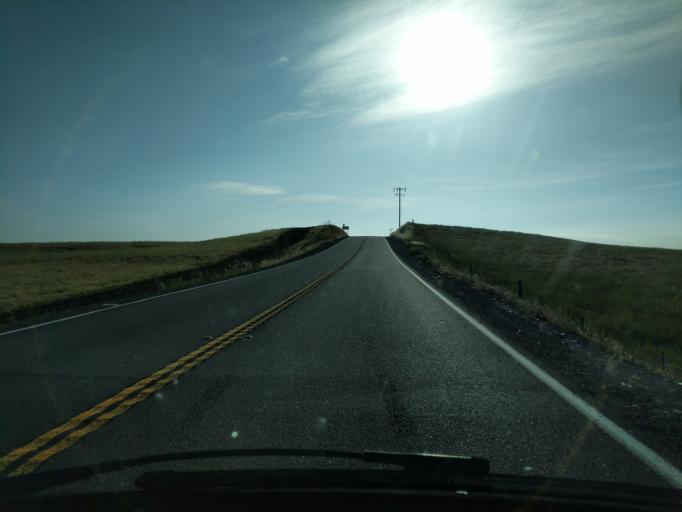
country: US
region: California
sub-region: Stanislaus County
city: East Oakdale
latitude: 37.9448
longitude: -120.8451
